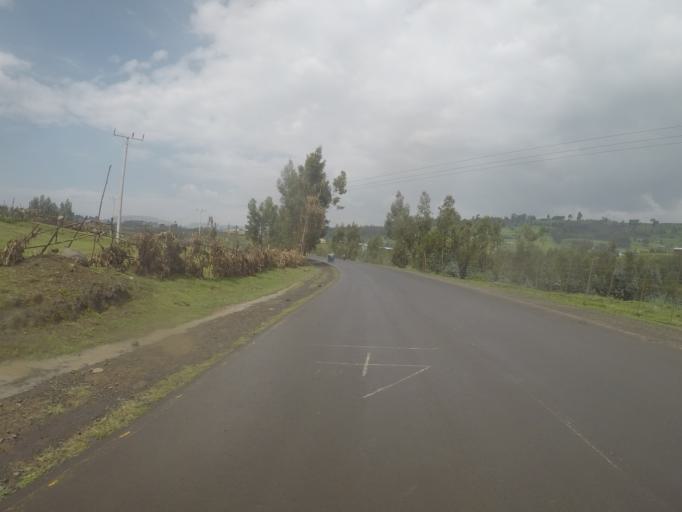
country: ET
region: Amhara
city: Debark'
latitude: 13.1283
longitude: 37.8895
